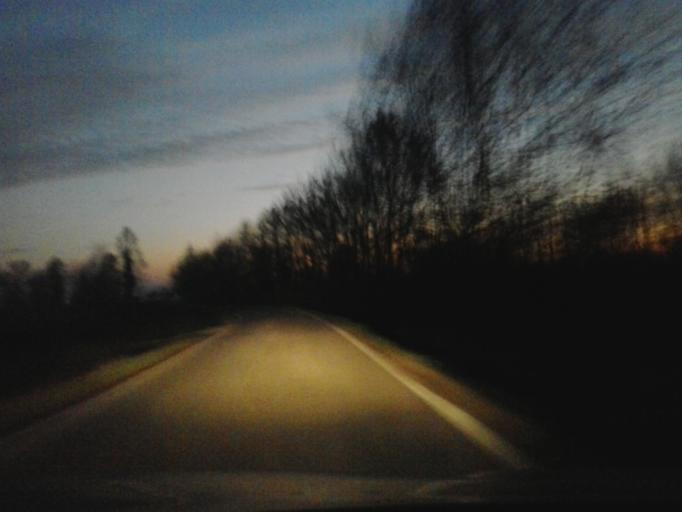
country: IT
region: Lombardy
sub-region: Provincia di Brescia
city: Azzano Mella
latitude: 45.4401
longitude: 10.1199
